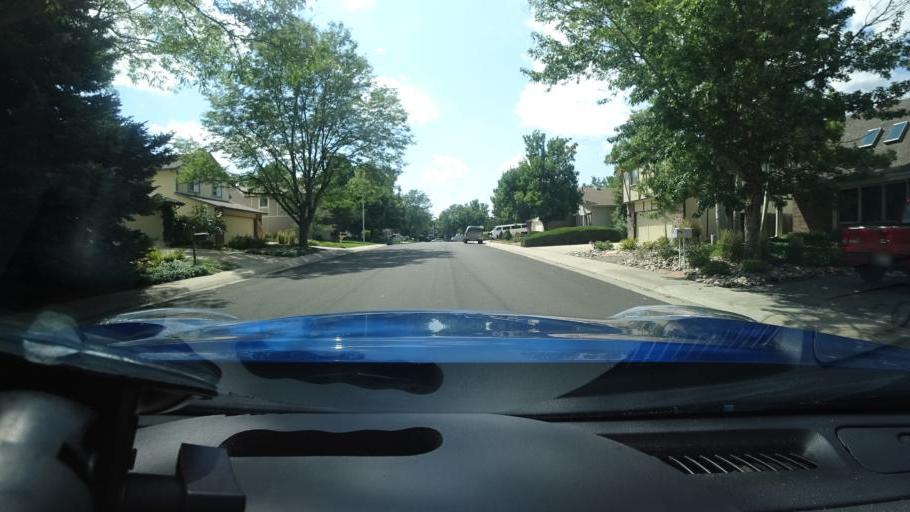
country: US
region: Colorado
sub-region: Adams County
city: Aurora
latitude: 39.6770
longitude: -104.8521
